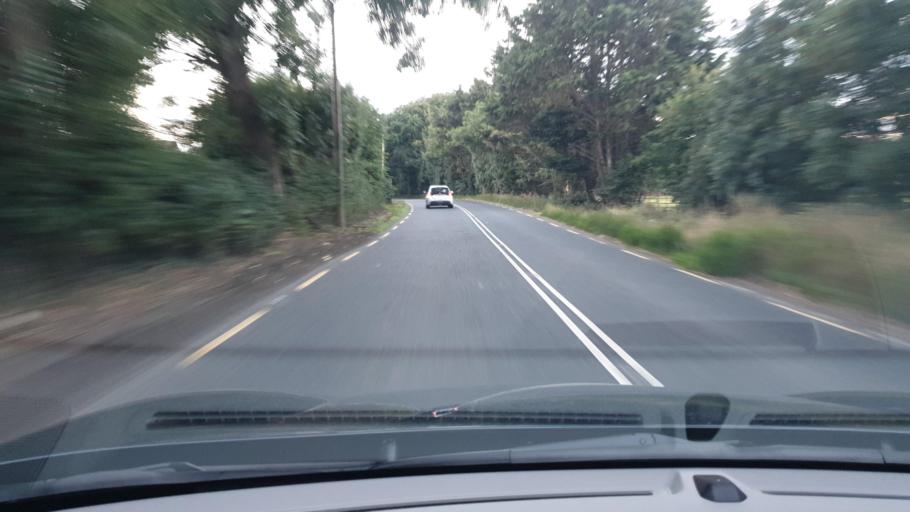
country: IE
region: Leinster
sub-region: An Mhi
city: Duleek
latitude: 53.6322
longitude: -6.4212
